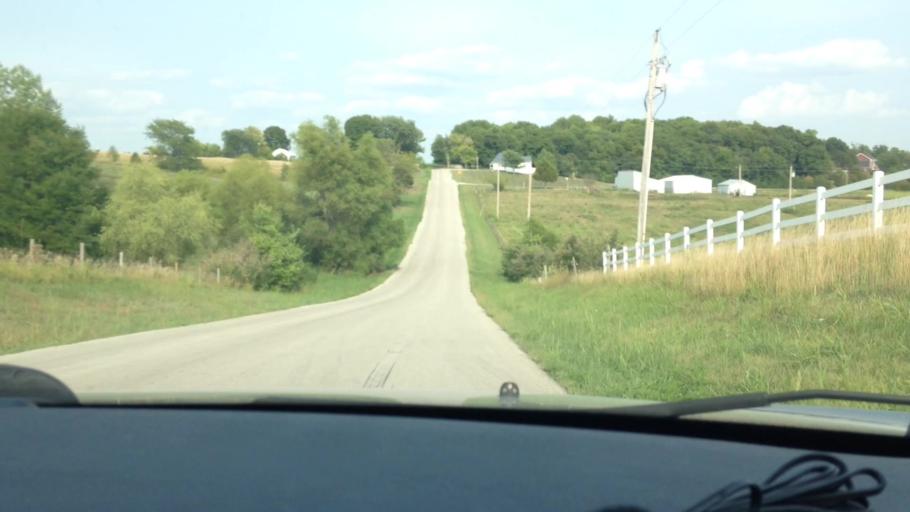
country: US
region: Missouri
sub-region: Platte County
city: Platte City
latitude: 39.4190
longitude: -94.7843
